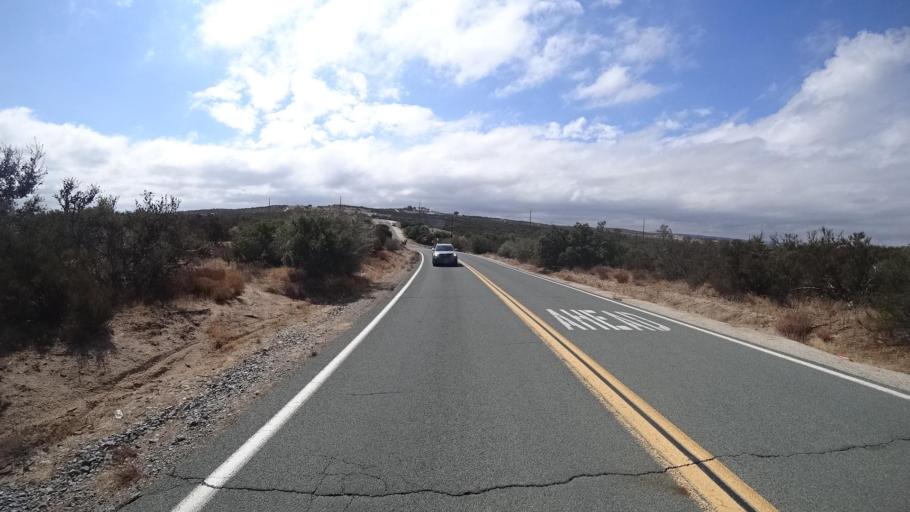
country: US
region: California
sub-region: San Diego County
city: Campo
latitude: 32.6666
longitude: -116.3166
